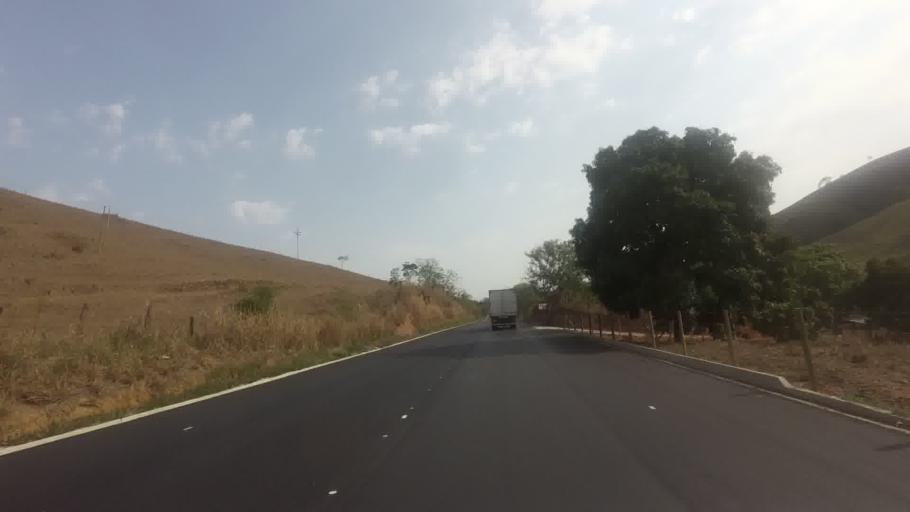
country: BR
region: Rio de Janeiro
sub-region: Bom Jesus Do Itabapoana
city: Bom Jesus do Itabapoana
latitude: -21.1748
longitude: -41.6830
